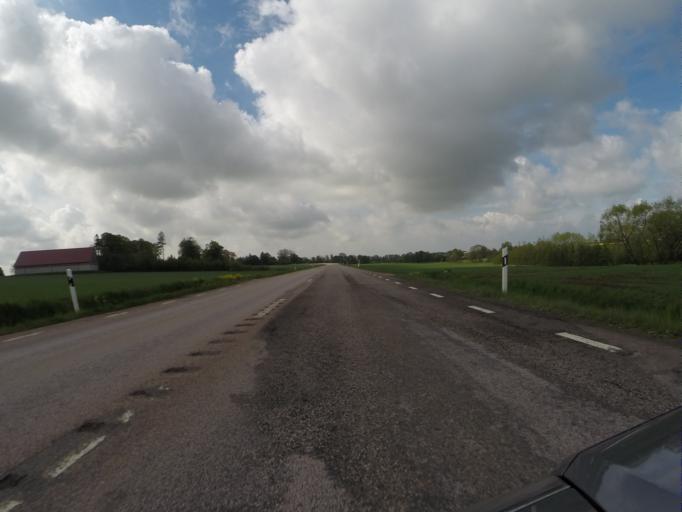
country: SE
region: Skane
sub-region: Bjuvs Kommun
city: Billesholm
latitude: 55.9856
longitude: 12.9382
